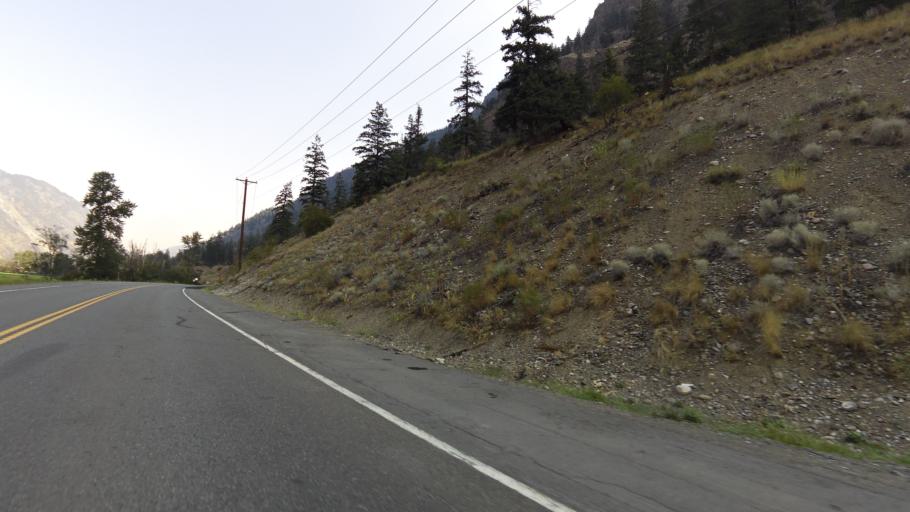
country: CA
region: British Columbia
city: Oliver
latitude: 49.2619
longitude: -120.0152
